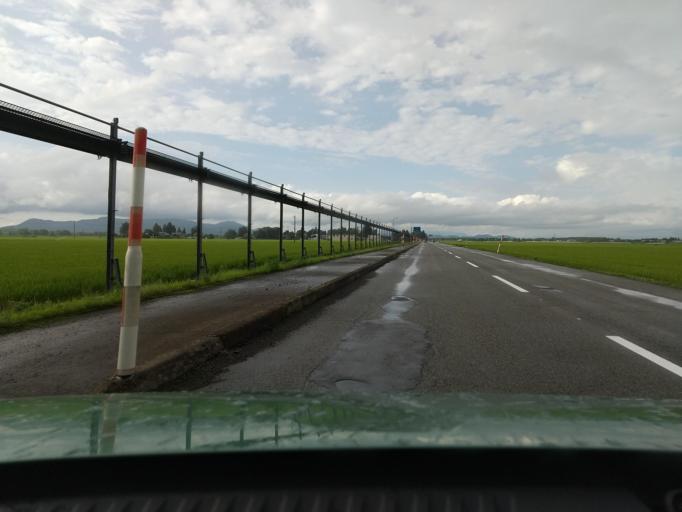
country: JP
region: Akita
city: Omagari
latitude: 39.3796
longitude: 140.4726
